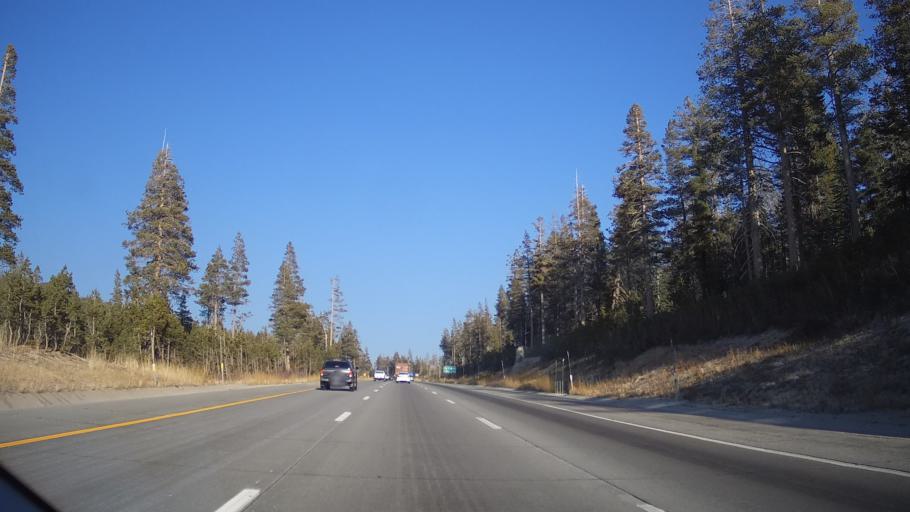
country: US
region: California
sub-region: Nevada County
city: Truckee
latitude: 39.3317
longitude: -120.3618
